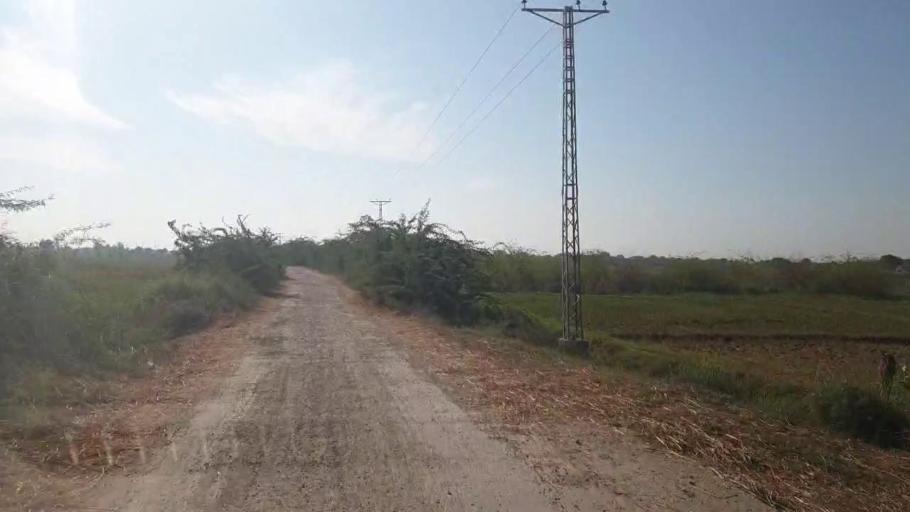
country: PK
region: Sindh
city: Talhar
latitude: 24.9436
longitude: 68.7937
